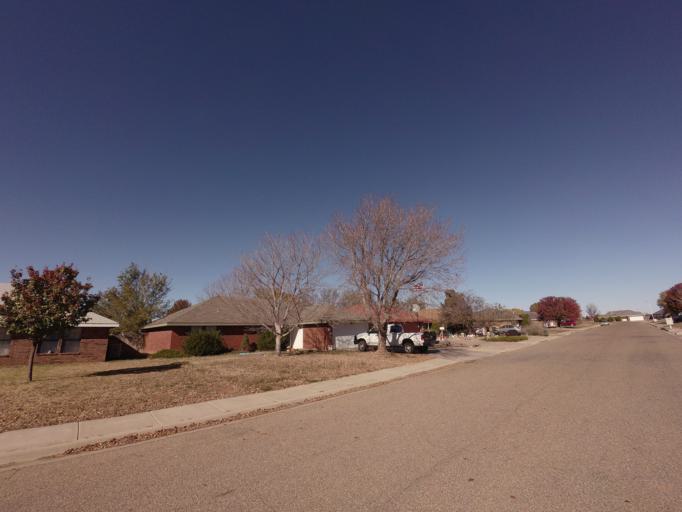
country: US
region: New Mexico
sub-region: Curry County
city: Clovis
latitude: 34.4137
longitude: -103.1674
